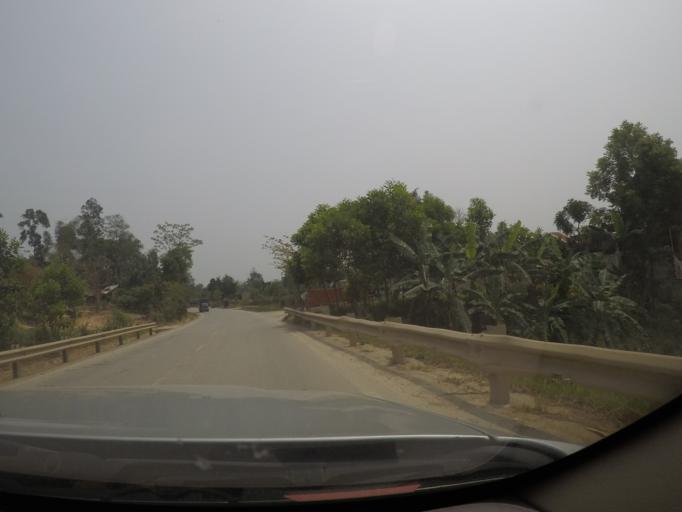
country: VN
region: Thanh Hoa
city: Thi Tran Yen Cat
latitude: 19.7065
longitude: 105.4418
